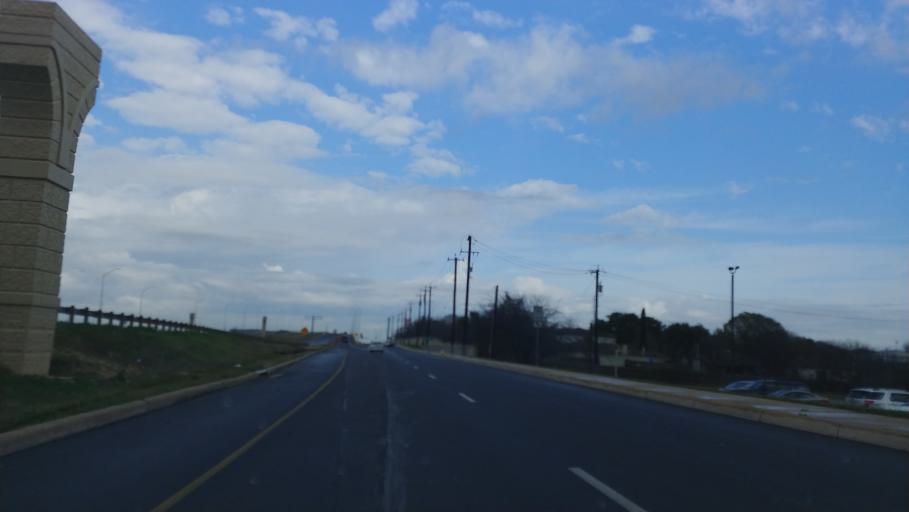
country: US
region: Texas
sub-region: Bexar County
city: Lackland Air Force Base
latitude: 29.3982
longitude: -98.7032
